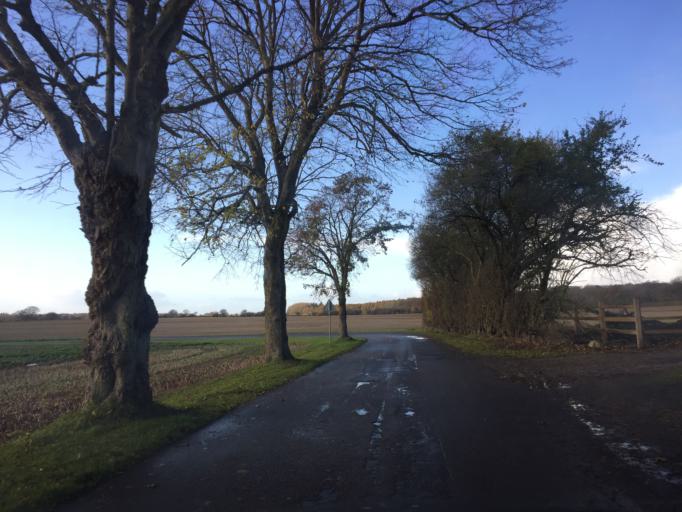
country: DK
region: South Denmark
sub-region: Kolding Kommune
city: Sonder Bjert
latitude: 55.4763
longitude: 9.6269
